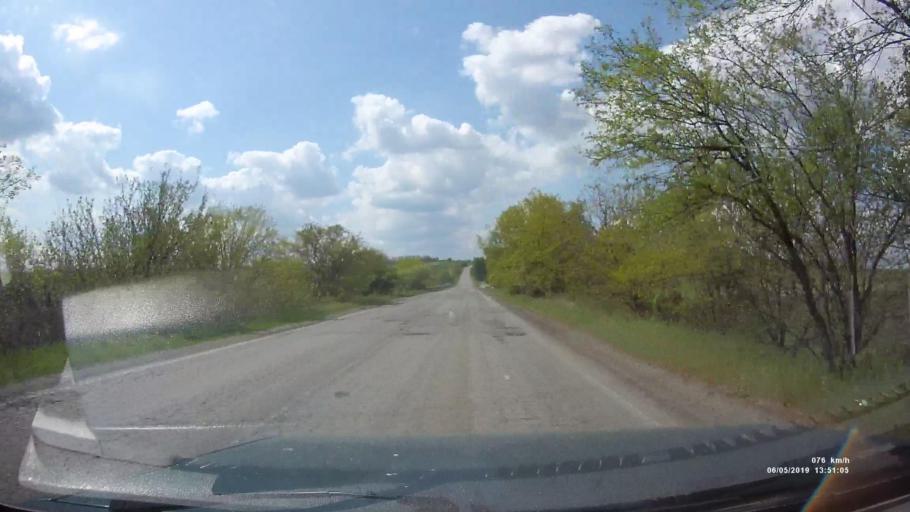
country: RU
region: Rostov
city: Melikhovskaya
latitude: 47.6557
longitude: 40.4977
